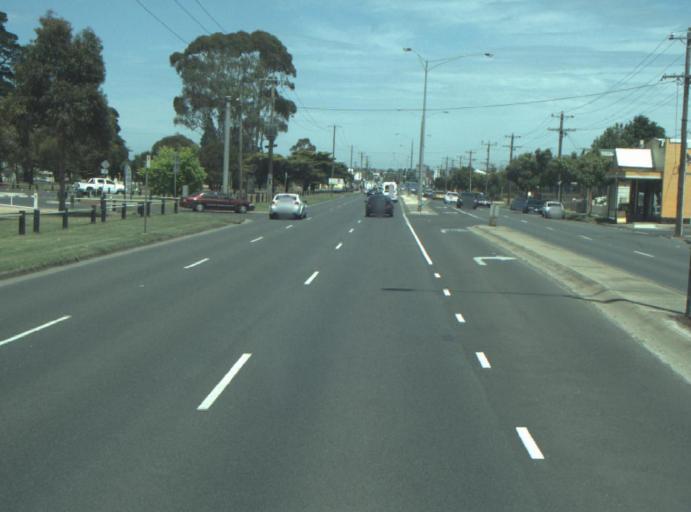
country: AU
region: Victoria
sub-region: Greater Geelong
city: Geelong
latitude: -38.1568
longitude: 144.3510
